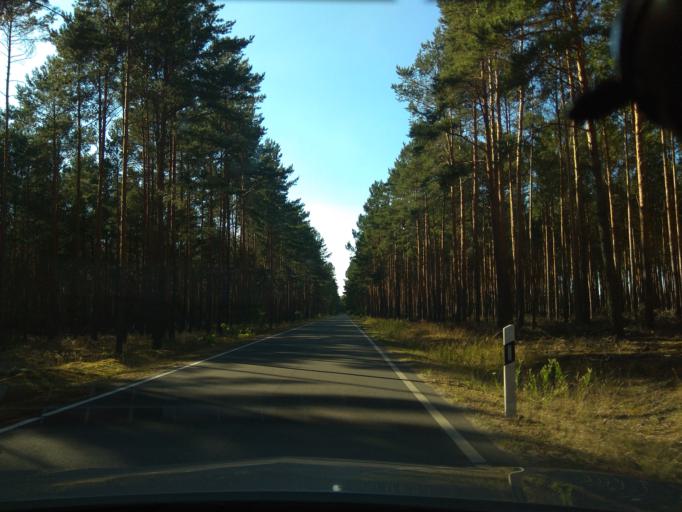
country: DE
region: Brandenburg
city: Baruth
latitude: 52.1201
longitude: 13.4993
